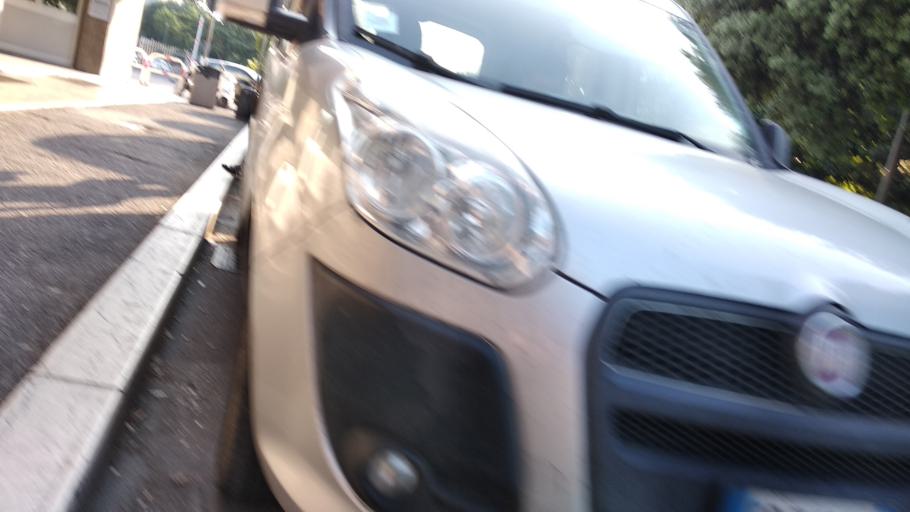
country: IT
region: Veneto
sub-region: Provincia di Verona
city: Verona
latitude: 45.4043
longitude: 10.9923
